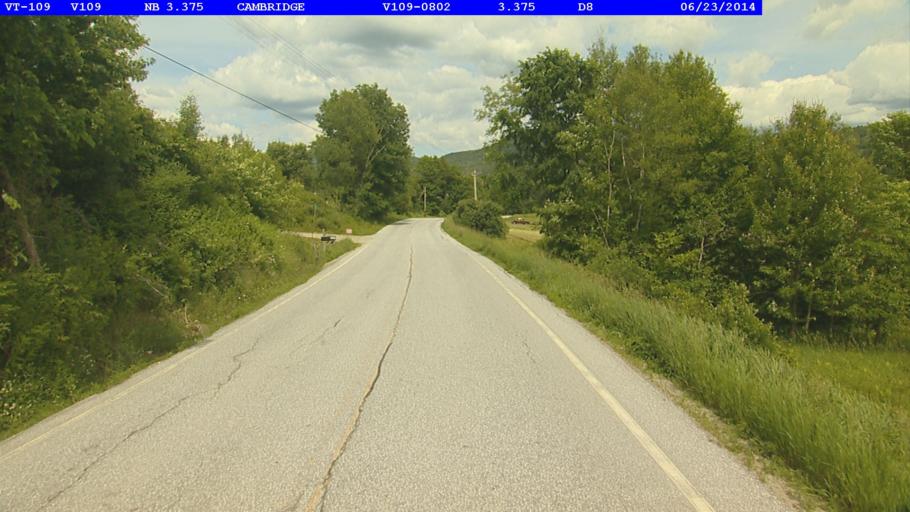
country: US
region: Vermont
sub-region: Lamoille County
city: Johnson
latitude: 44.6814
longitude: -72.7801
